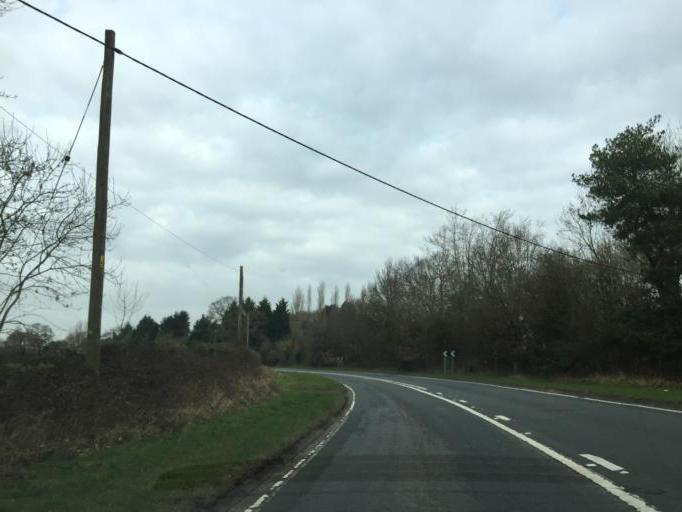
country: GB
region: England
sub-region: Warwickshire
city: Henley in Arden
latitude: 52.2973
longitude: -1.8277
